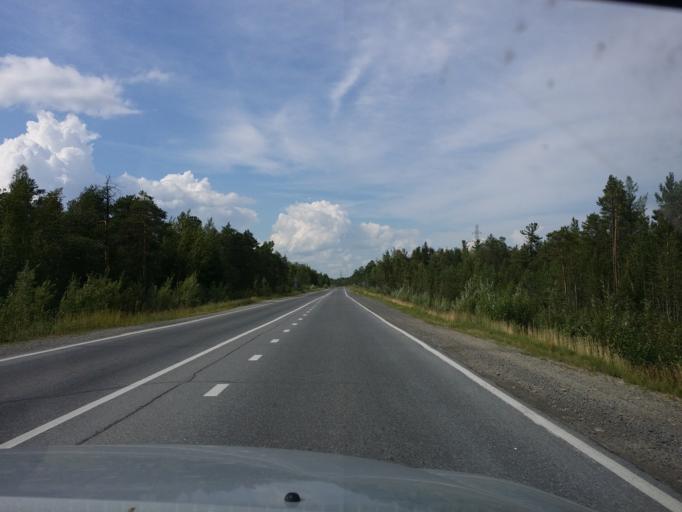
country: RU
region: Khanty-Mansiyskiy Avtonomnyy Okrug
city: Megion
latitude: 61.1348
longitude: 75.7667
